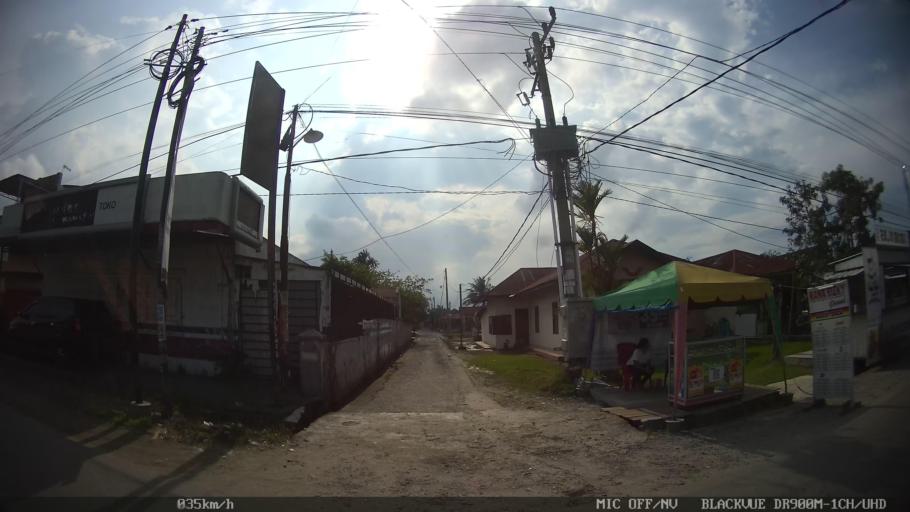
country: ID
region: North Sumatra
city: Medan
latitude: 3.5841
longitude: 98.7567
